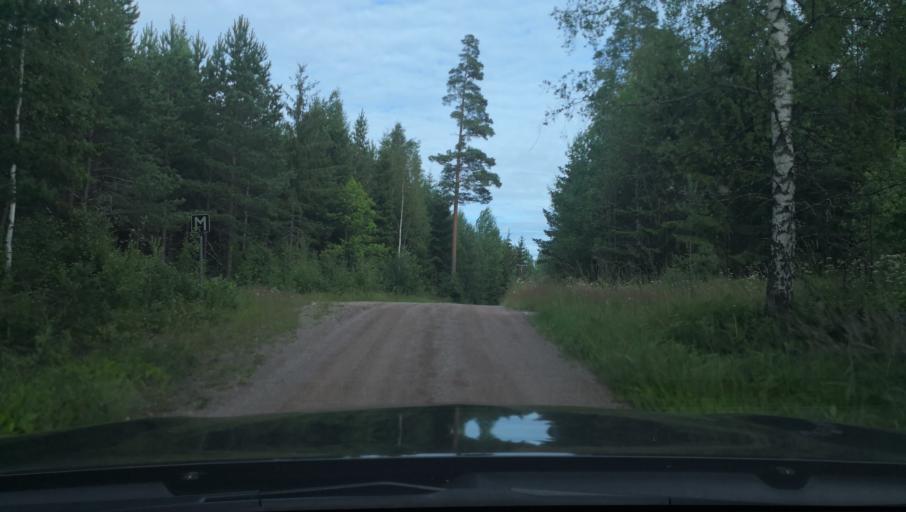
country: SE
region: Vaestmanland
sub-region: Surahammars Kommun
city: Surahammar
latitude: 59.6582
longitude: 16.1348
